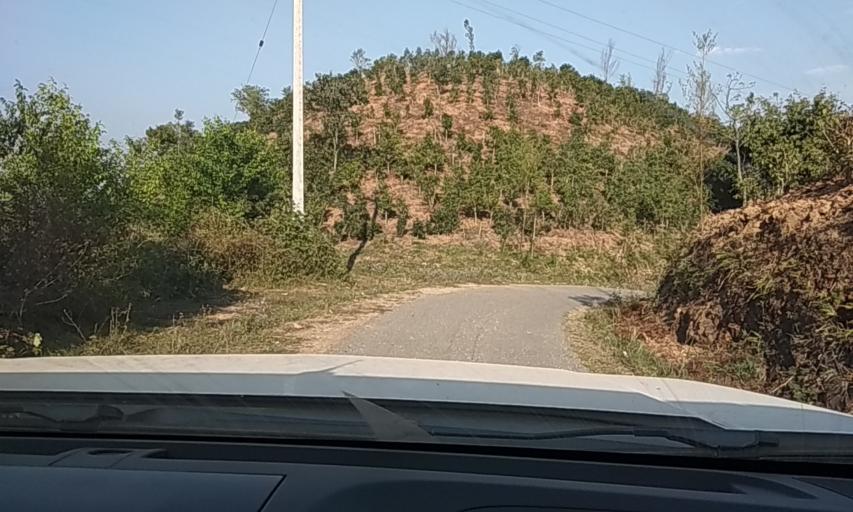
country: LA
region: Phongsali
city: Phongsali
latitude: 21.6592
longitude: 102.1679
